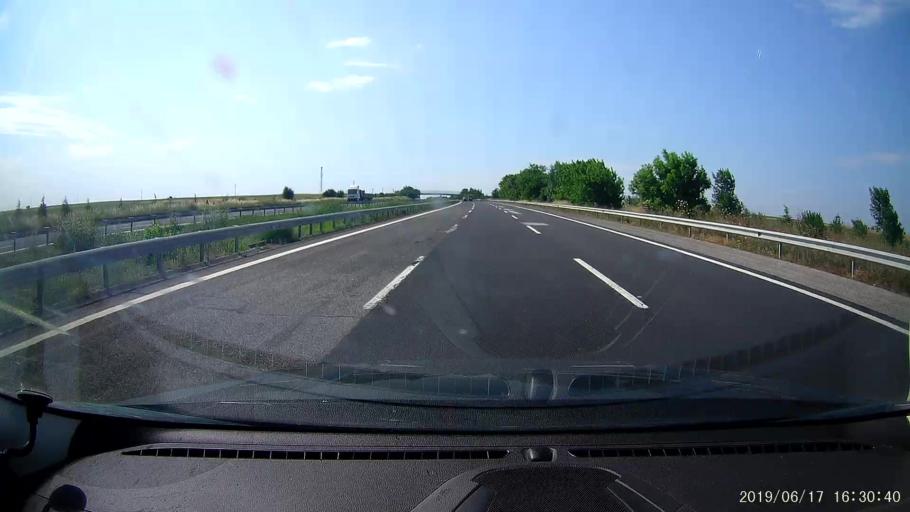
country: TR
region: Tekirdag
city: Beyazkoy
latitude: 41.3510
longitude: 27.6483
